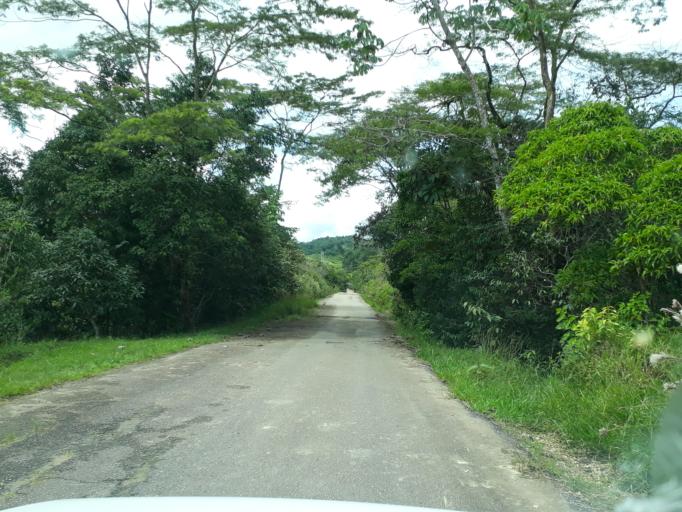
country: CO
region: Cundinamarca
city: Medina
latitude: 4.6007
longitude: -73.2980
